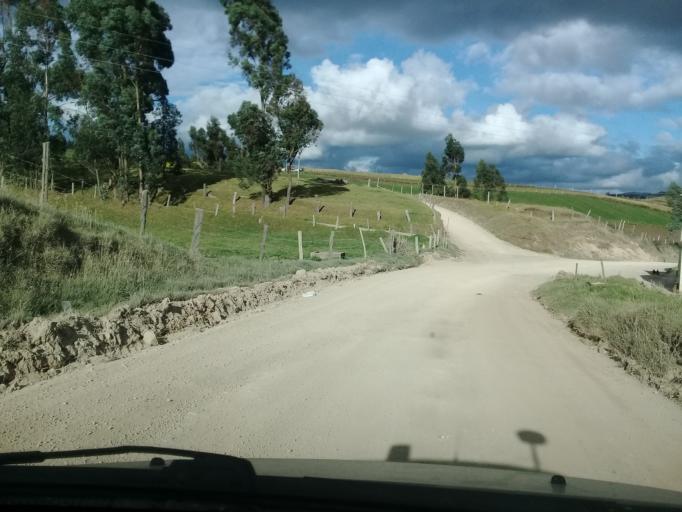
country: CO
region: Cundinamarca
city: Lenguazaque
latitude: 5.2789
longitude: -73.6581
